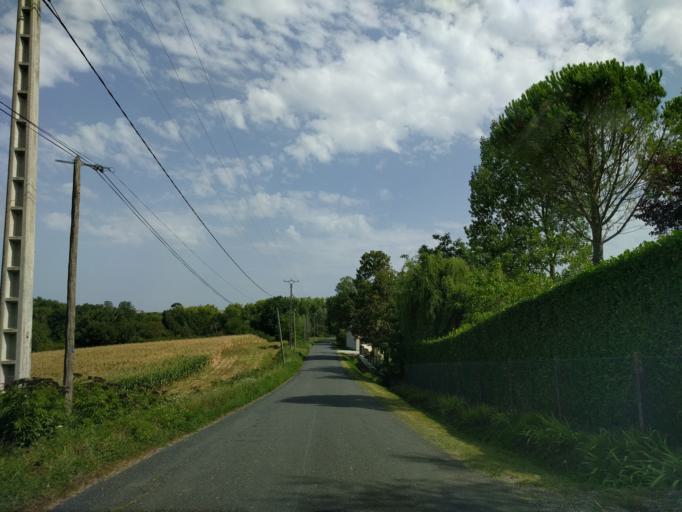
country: FR
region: Midi-Pyrenees
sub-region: Departement du Tarn
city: Saix
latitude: 43.6384
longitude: 2.1868
